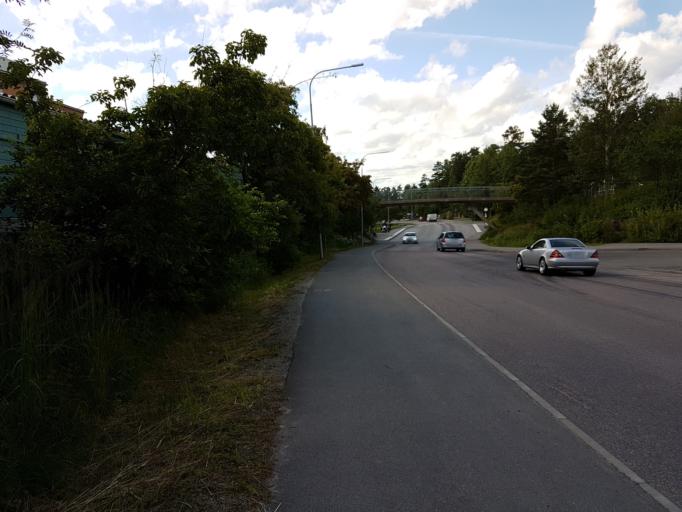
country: SE
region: Stockholm
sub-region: Nacka Kommun
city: Boo
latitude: 59.3320
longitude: 18.2652
